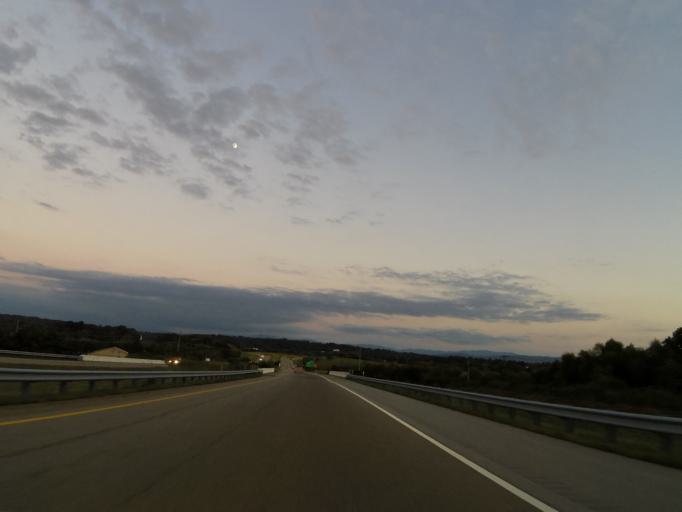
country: US
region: Tennessee
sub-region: Blount County
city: Eagleton Village
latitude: 35.8131
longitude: -83.9477
